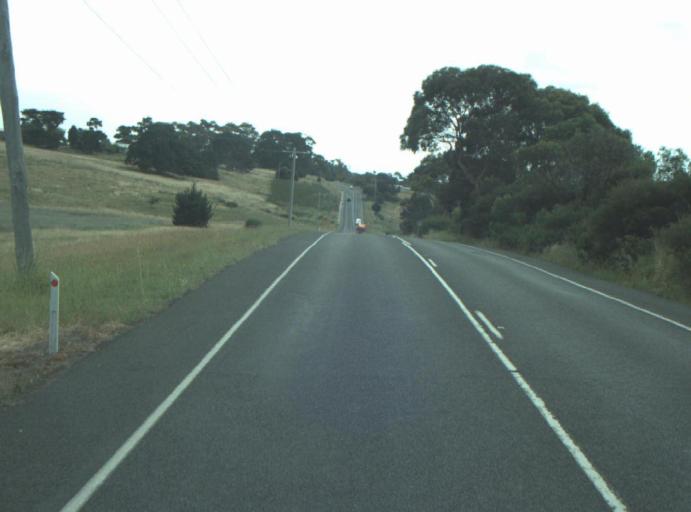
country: AU
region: Victoria
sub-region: Greater Geelong
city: Leopold
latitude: -38.2497
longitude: 144.5042
